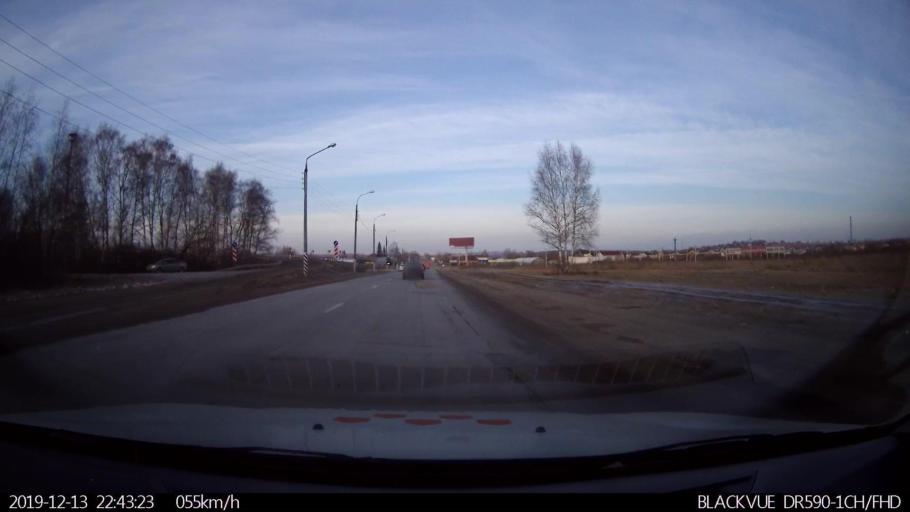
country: RU
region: Nizjnij Novgorod
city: Afonino
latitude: 56.1960
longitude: 44.1244
